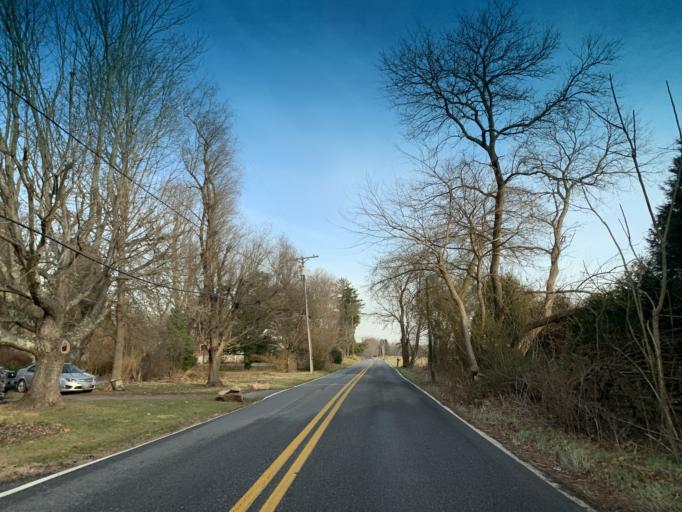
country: US
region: Maryland
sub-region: Harford County
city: Jarrettsville
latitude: 39.5574
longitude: -76.5624
